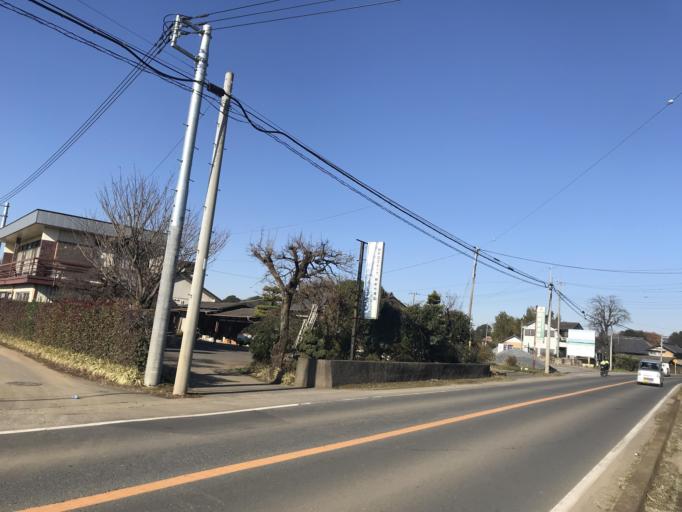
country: JP
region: Tochigi
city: Oyama
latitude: 36.2211
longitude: 139.8246
